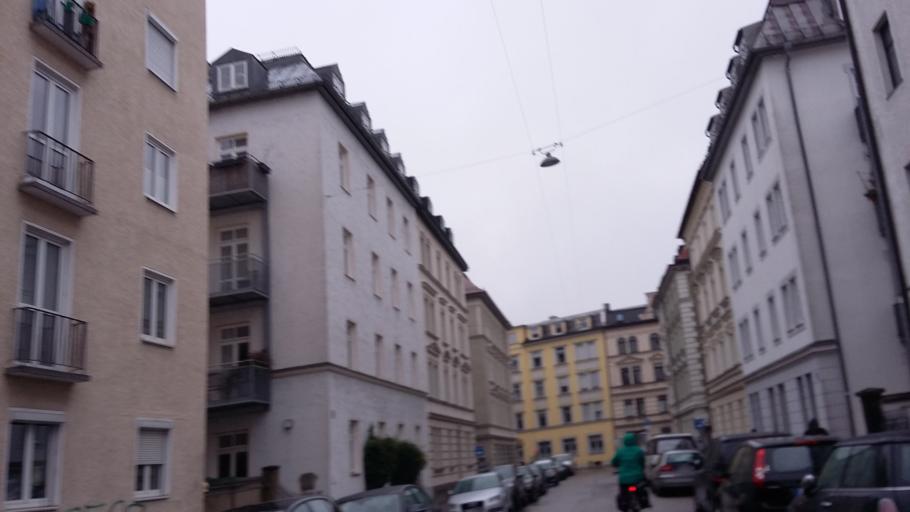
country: DE
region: Bavaria
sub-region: Upper Bavaria
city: Munich
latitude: 48.1245
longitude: 11.5540
